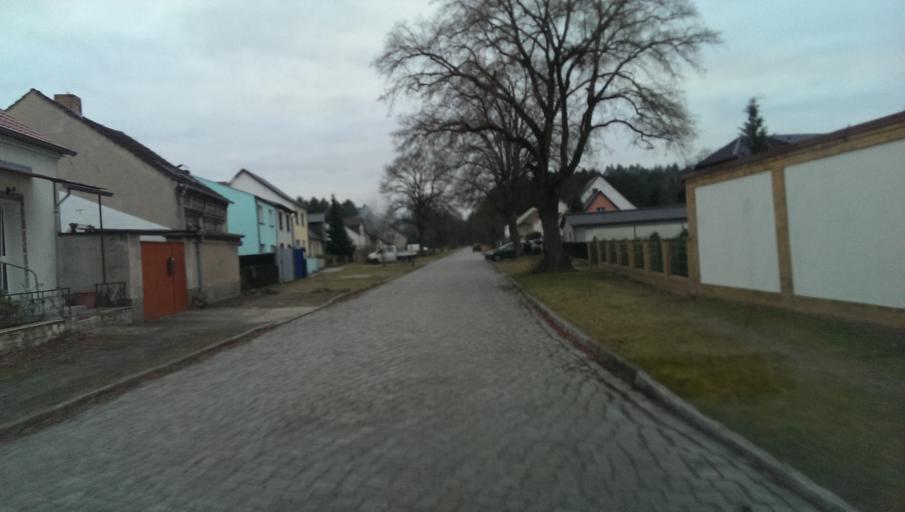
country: DE
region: Brandenburg
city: Sperenberg
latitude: 52.1567
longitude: 13.3395
